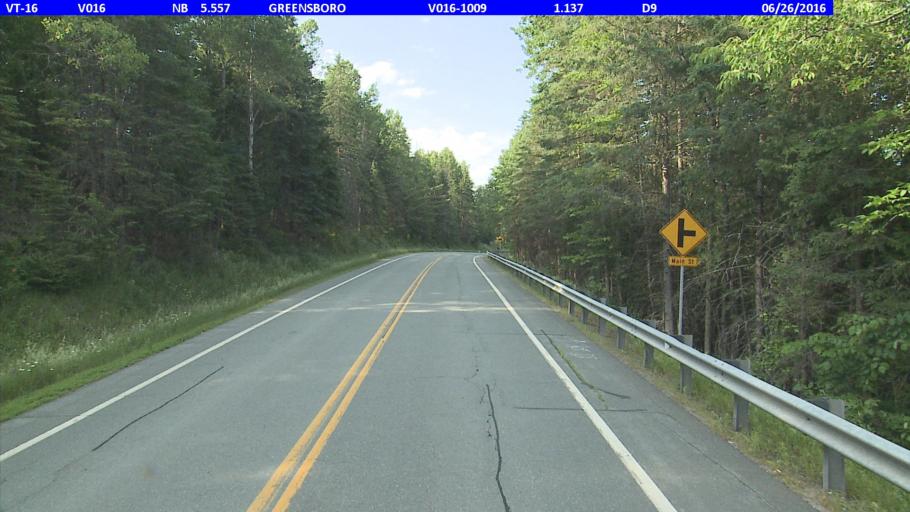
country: US
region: Vermont
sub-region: Caledonia County
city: Hardwick
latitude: 44.5590
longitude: -72.2581
